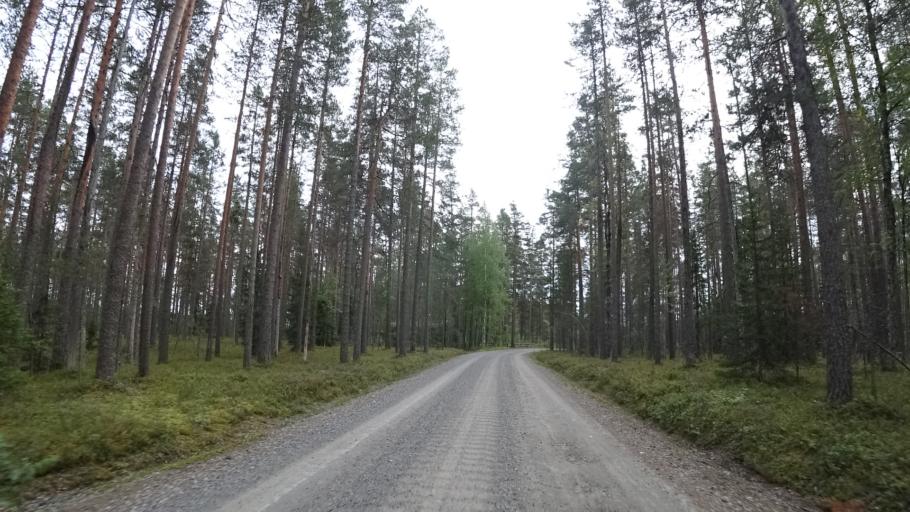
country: FI
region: North Karelia
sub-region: Joensuu
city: Ilomantsi
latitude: 62.5999
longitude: 31.1876
